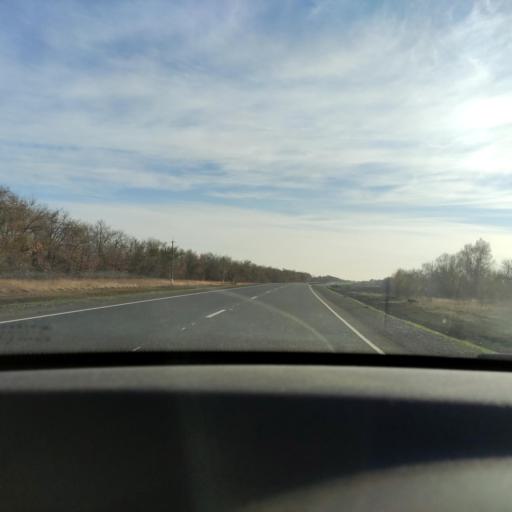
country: RU
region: Samara
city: Krasnoarmeyskoye
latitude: 52.8343
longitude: 50.0056
